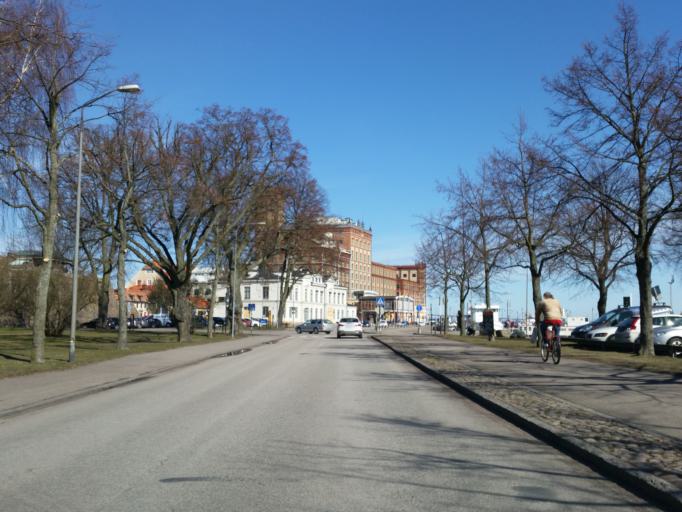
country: SE
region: Kalmar
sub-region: Kalmar Kommun
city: Kalmar
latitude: 56.6622
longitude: 16.3671
